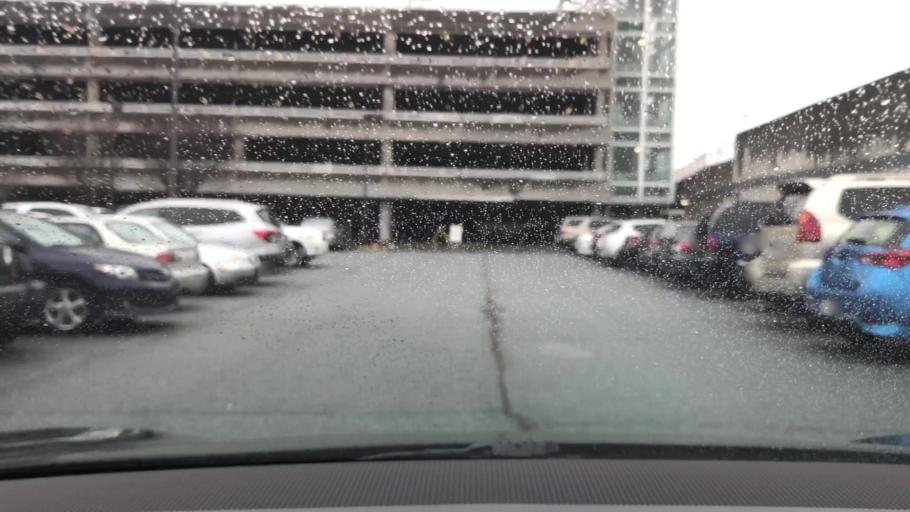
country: US
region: Georgia
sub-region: DeKalb County
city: Doraville
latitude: 33.9018
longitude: -84.2815
